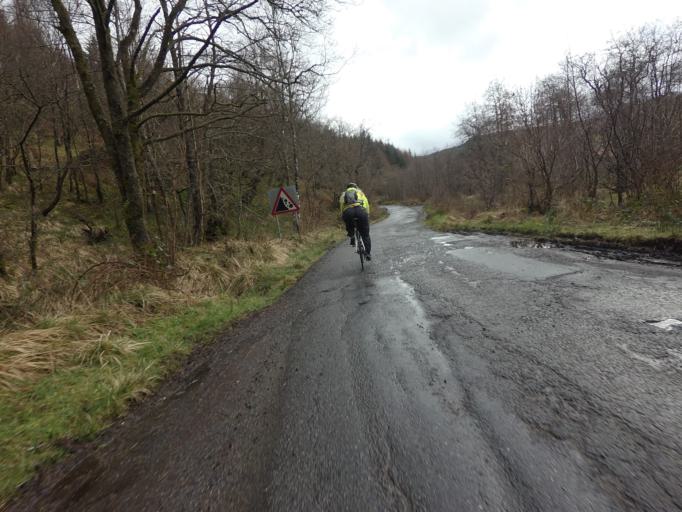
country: GB
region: Scotland
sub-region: West Dunbartonshire
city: Balloch
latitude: 56.2052
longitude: -4.5299
